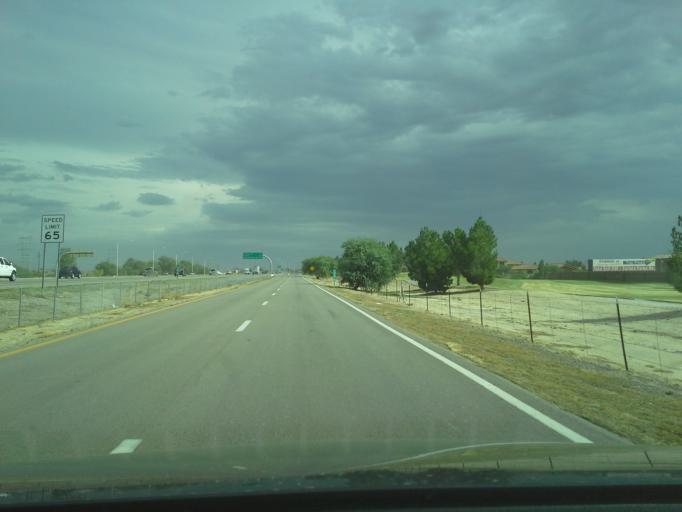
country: US
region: Arizona
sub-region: Pima County
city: Tortolita
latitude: 32.3672
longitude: -111.0990
